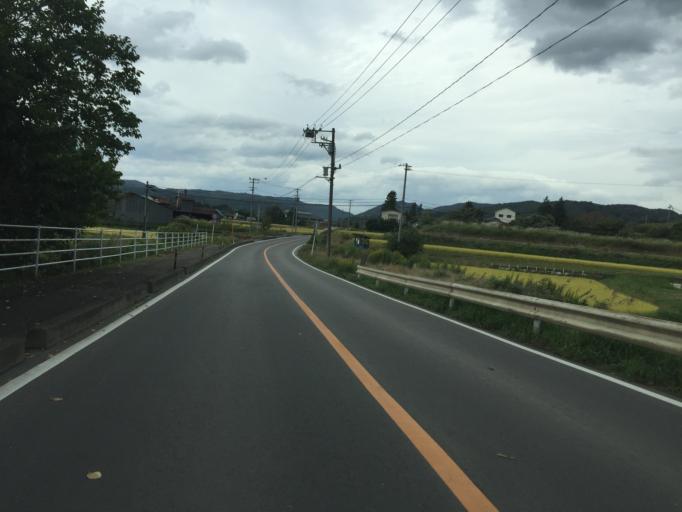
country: JP
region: Fukushima
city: Yanagawamachi-saiwaicho
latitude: 37.8675
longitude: 140.6227
